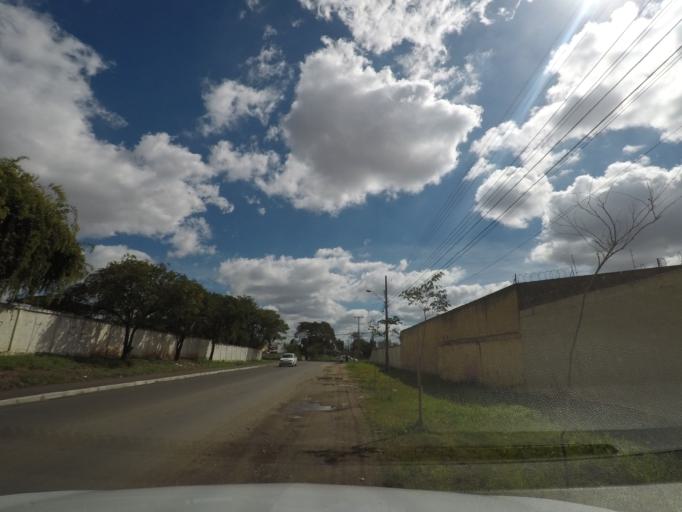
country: BR
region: Parana
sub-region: Sao Jose Dos Pinhais
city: Sao Jose dos Pinhais
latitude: -25.4931
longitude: -49.2320
